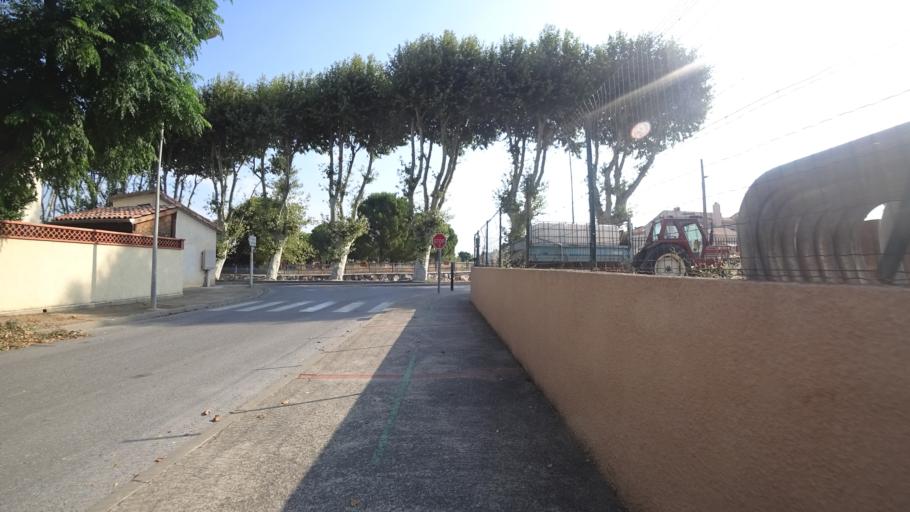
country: FR
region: Languedoc-Roussillon
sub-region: Departement des Pyrenees-Orientales
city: Claira
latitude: 42.7598
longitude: 2.9526
